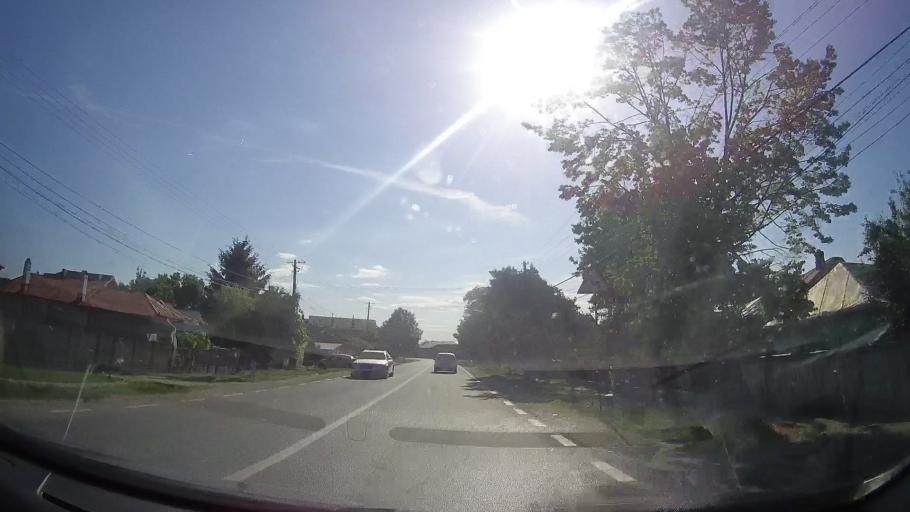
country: RO
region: Prahova
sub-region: Comuna Berceni
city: Corlatesti
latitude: 44.9134
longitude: 26.0875
